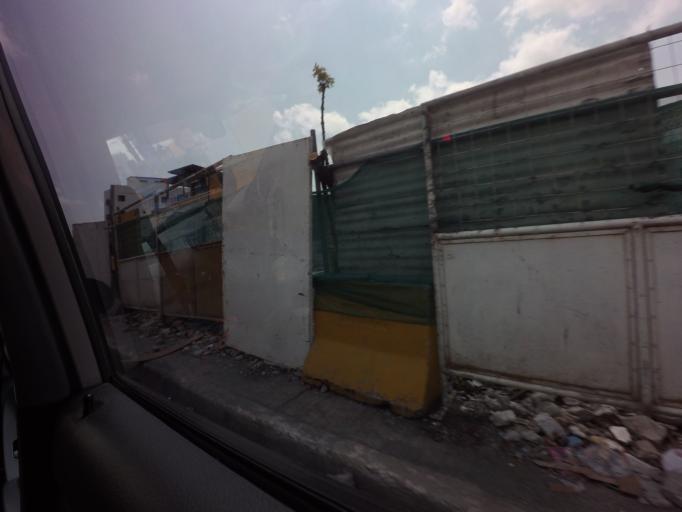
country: PH
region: Metro Manila
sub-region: City of Manila
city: Quiapo
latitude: 14.5845
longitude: 121.0034
